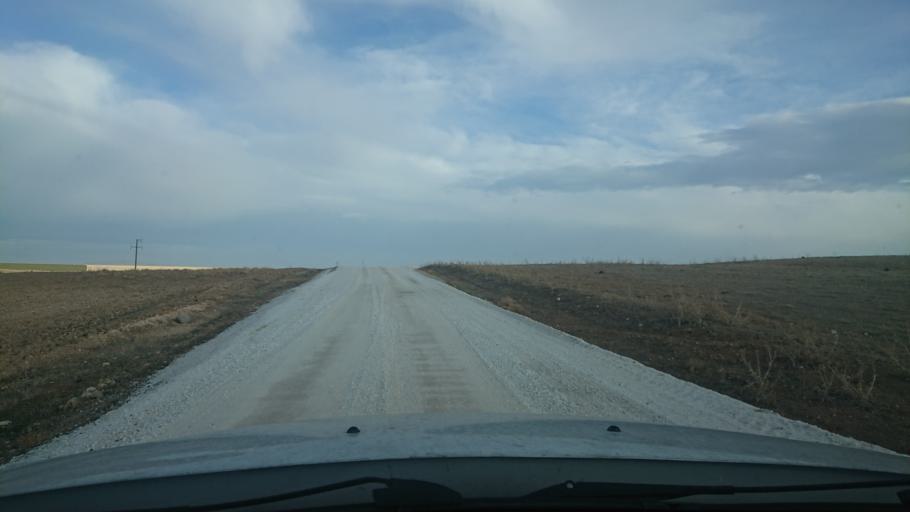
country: TR
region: Aksaray
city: Agacoren
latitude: 38.7355
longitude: 33.8695
